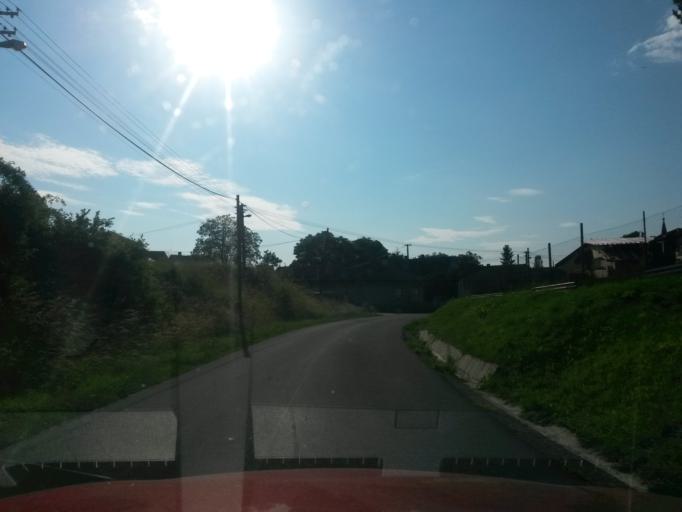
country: SK
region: Presovsky
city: Sabinov
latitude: 49.0635
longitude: 21.0587
